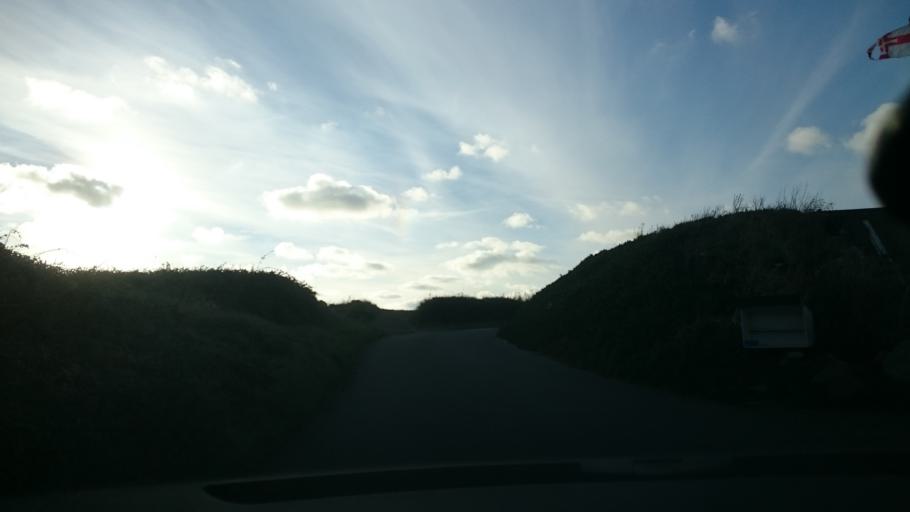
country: GG
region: St Peter Port
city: Saint Peter Port
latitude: 49.4550
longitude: -2.6541
